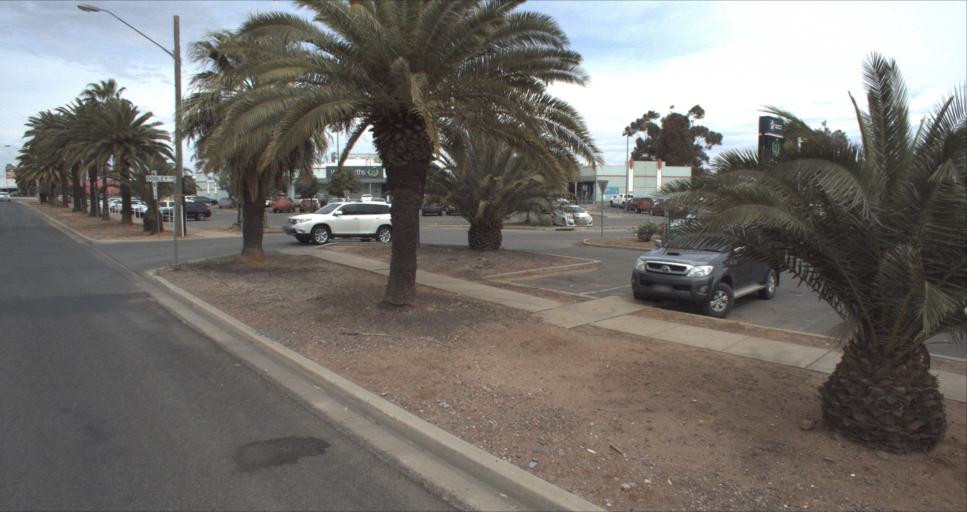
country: AU
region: New South Wales
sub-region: Leeton
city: Leeton
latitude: -34.5502
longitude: 146.3994
